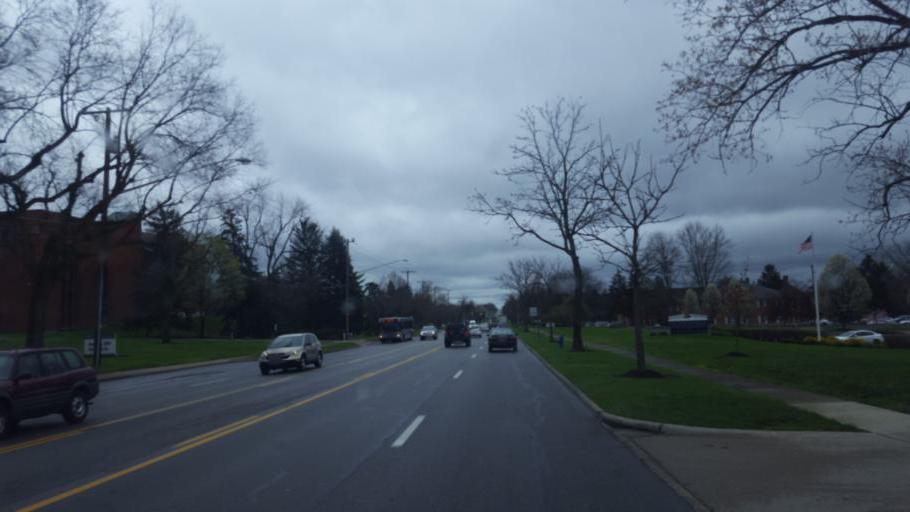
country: US
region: Ohio
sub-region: Franklin County
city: Worthington
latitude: 40.1017
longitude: -83.0173
